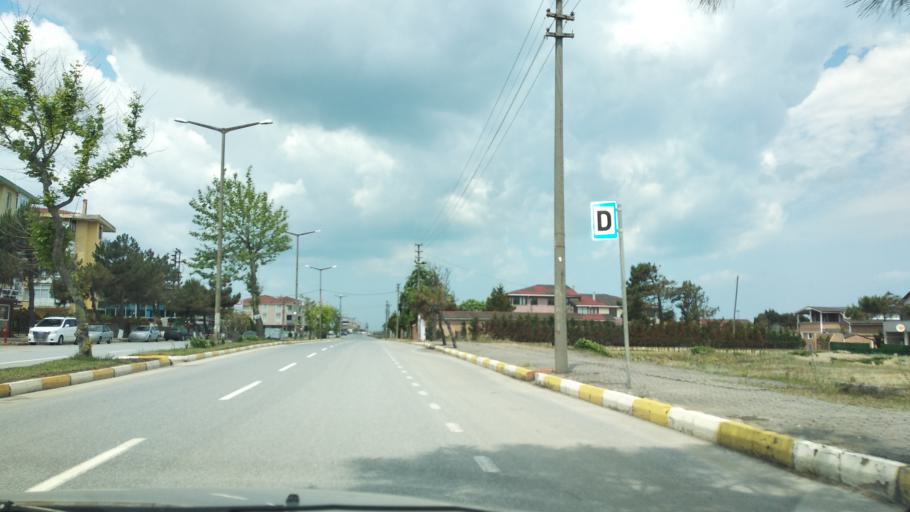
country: TR
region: Sakarya
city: Karasu
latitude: 41.1127
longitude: 30.6855
